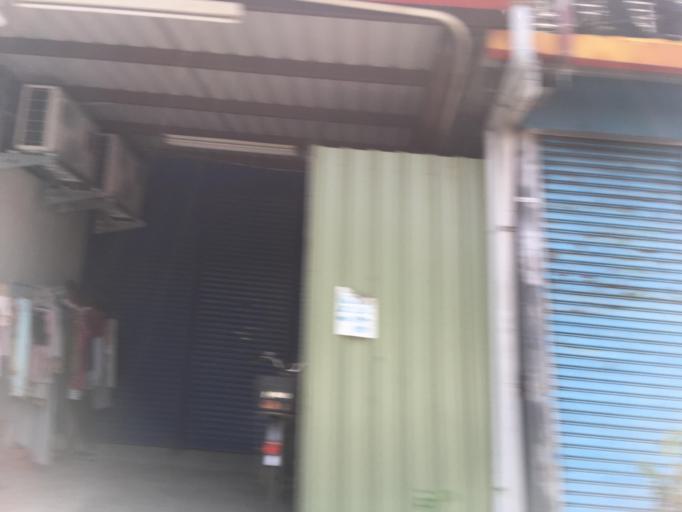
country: TW
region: Taiwan
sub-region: Yilan
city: Yilan
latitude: 24.6544
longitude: 121.7639
